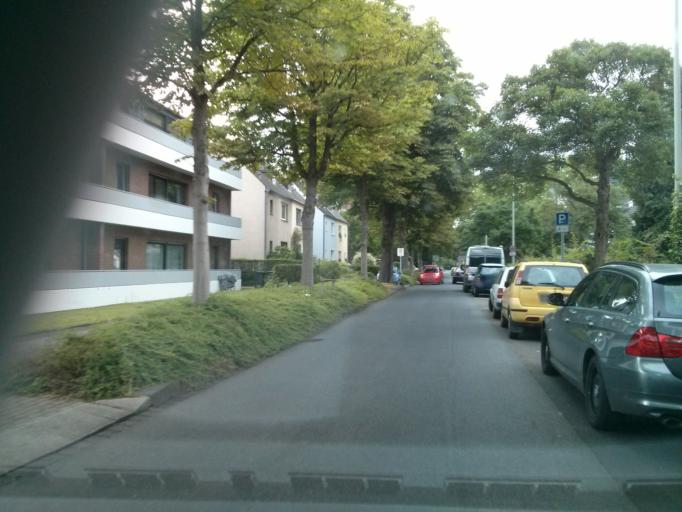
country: DE
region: North Rhine-Westphalia
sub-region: Regierungsbezirk Dusseldorf
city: Krefeld
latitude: 51.3438
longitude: 6.5937
